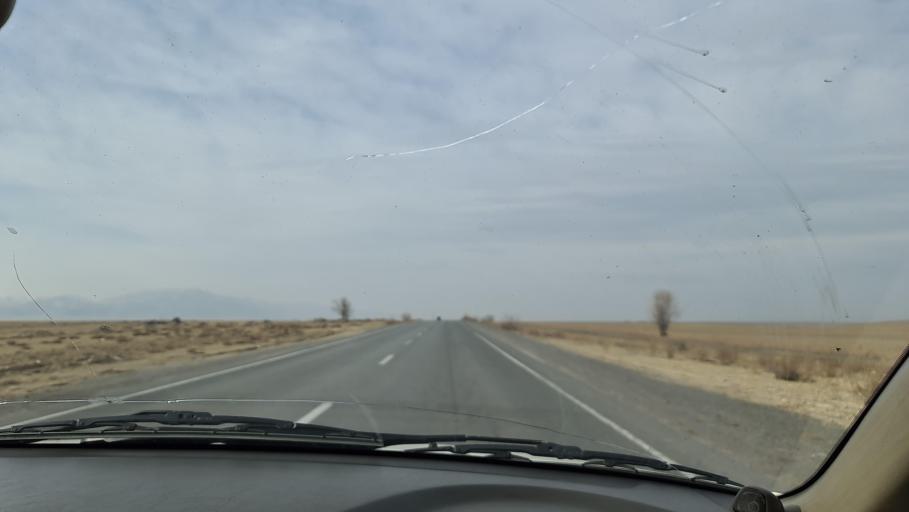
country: KG
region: Chuy
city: Bystrovka
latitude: 43.3231
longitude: 75.7100
